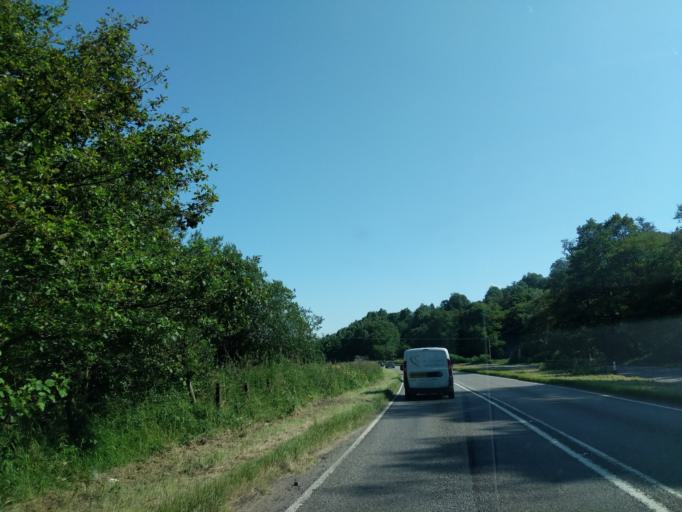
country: GB
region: Scotland
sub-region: Moray
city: Rothes
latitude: 57.5106
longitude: -3.2039
